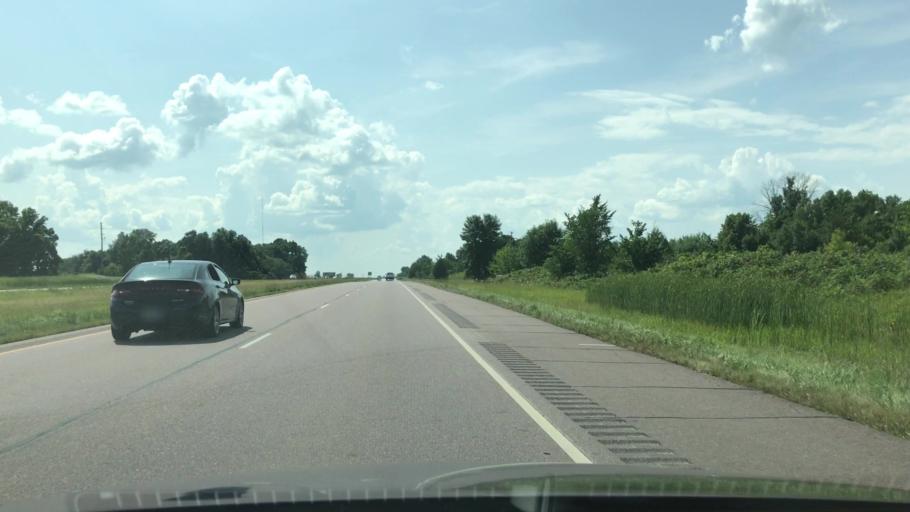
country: US
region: Minnesota
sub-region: Nicollet County
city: North Mankato
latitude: 44.1447
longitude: -94.0965
